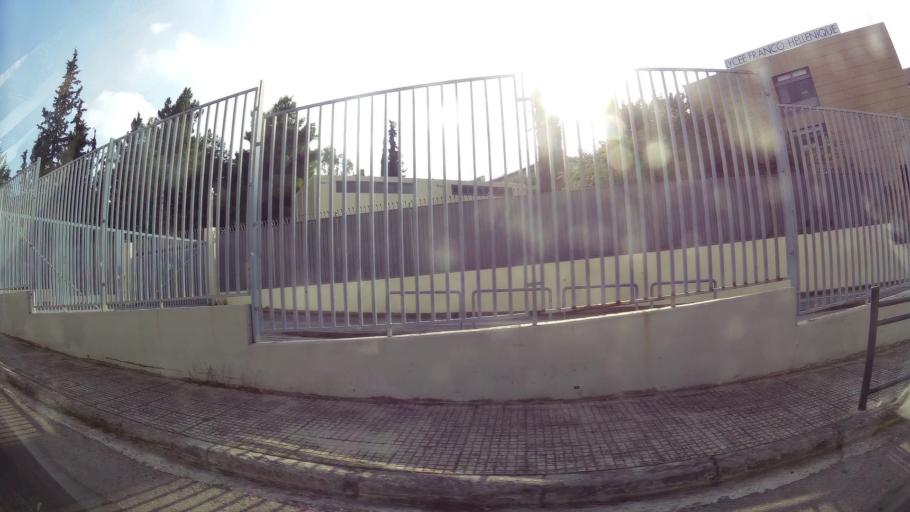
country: GR
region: Attica
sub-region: Nomarchia Athinas
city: Agia Paraskevi
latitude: 38.0104
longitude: 23.8372
